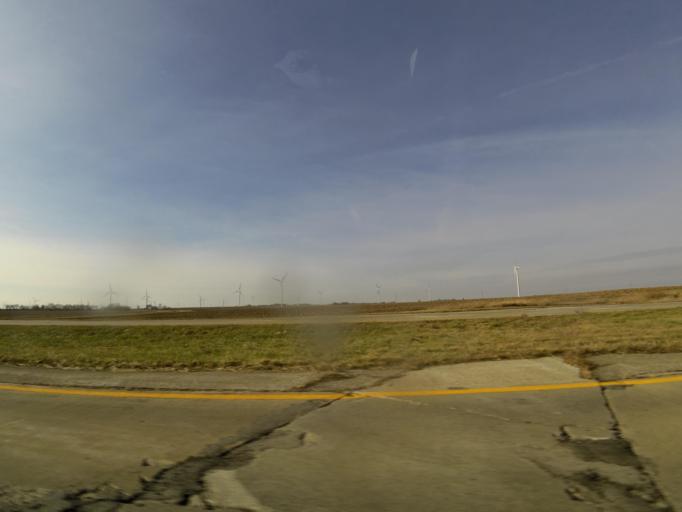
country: US
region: Illinois
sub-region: Macon County
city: Maroa
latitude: 40.0461
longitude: -88.9657
